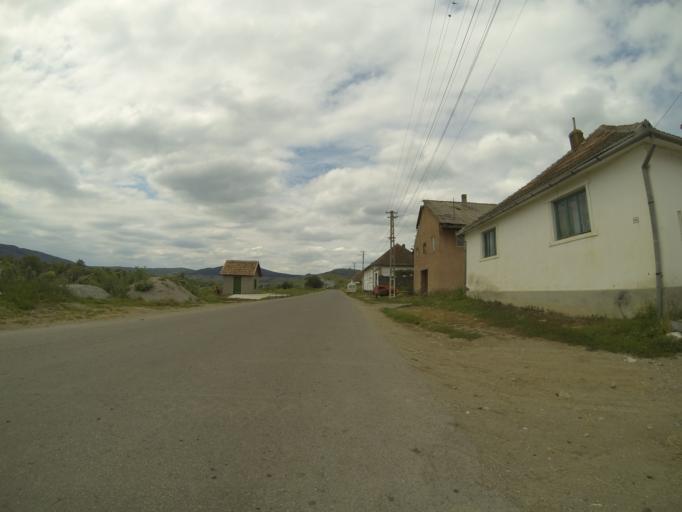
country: RO
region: Brasov
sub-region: Comuna Hoghiz
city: Hoghiz
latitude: 46.0260
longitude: 25.3992
